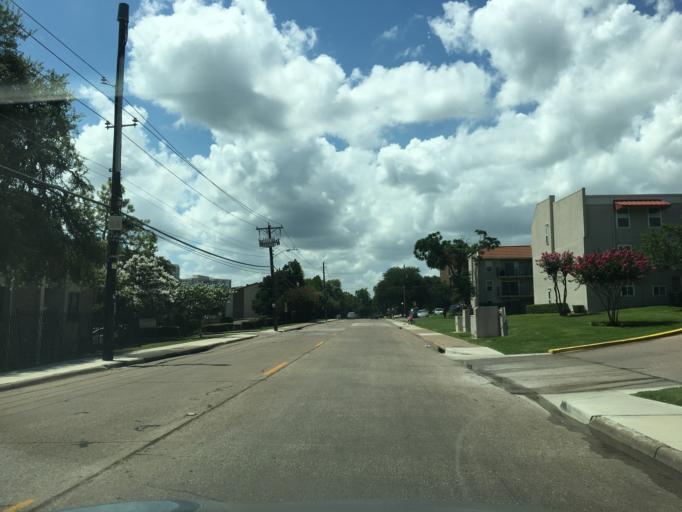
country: US
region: Texas
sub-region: Dallas County
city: University Park
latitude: 32.8668
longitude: -96.7590
